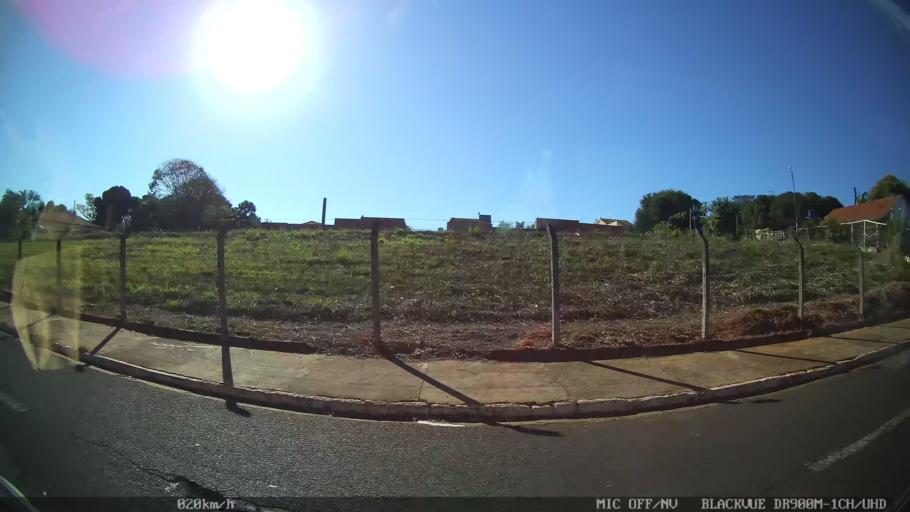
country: BR
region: Sao Paulo
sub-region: Olimpia
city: Olimpia
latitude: -20.7432
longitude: -48.9002
